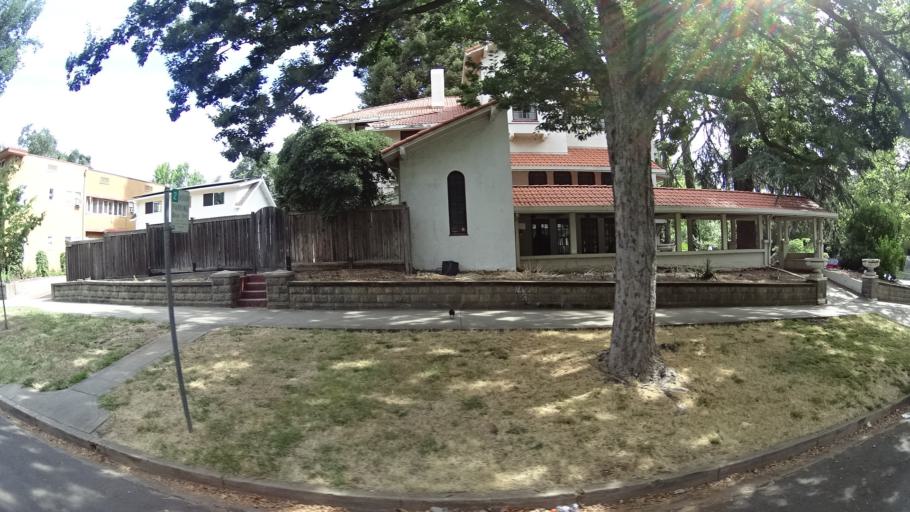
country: US
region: California
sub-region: Sacramento County
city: Sacramento
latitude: 38.5629
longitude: -121.4834
